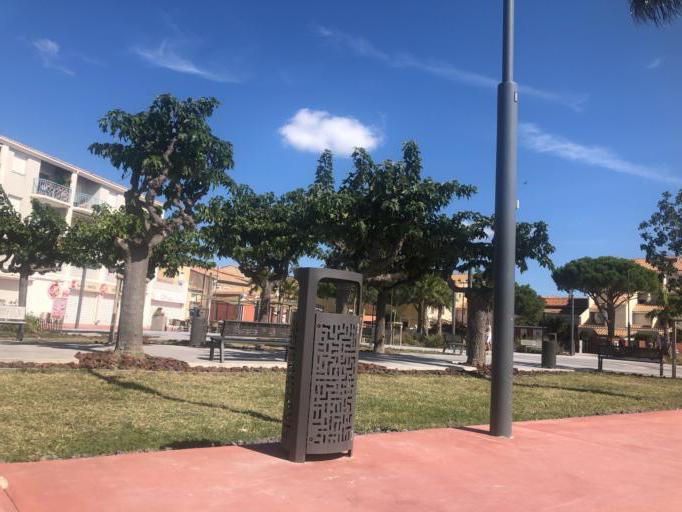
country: FR
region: Languedoc-Roussillon
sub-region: Departement de l'Herault
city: Meze
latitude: 43.4227
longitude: 3.6075
